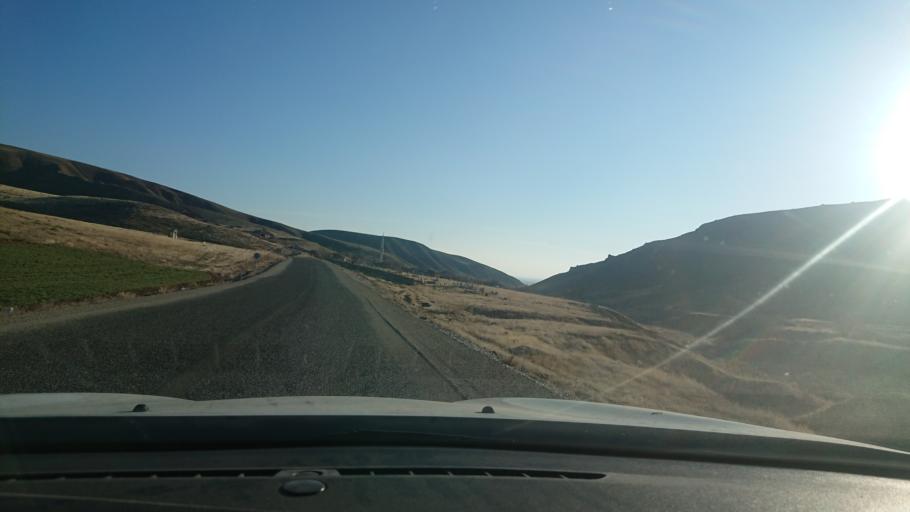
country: TR
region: Aksaray
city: Acipinar
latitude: 38.6958
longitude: 33.7489
